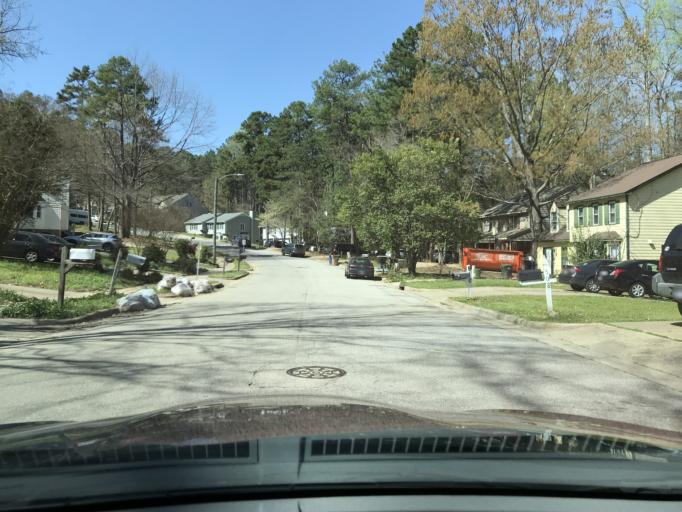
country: US
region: North Carolina
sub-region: Wake County
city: West Raleigh
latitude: 35.7731
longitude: -78.6943
